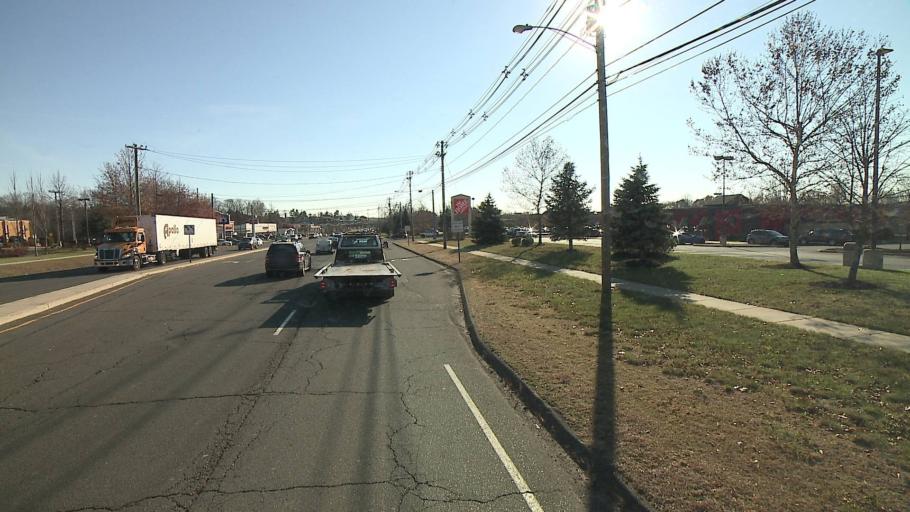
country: US
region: Connecticut
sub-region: New Haven County
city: Meriden
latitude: 41.4972
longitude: -72.8099
